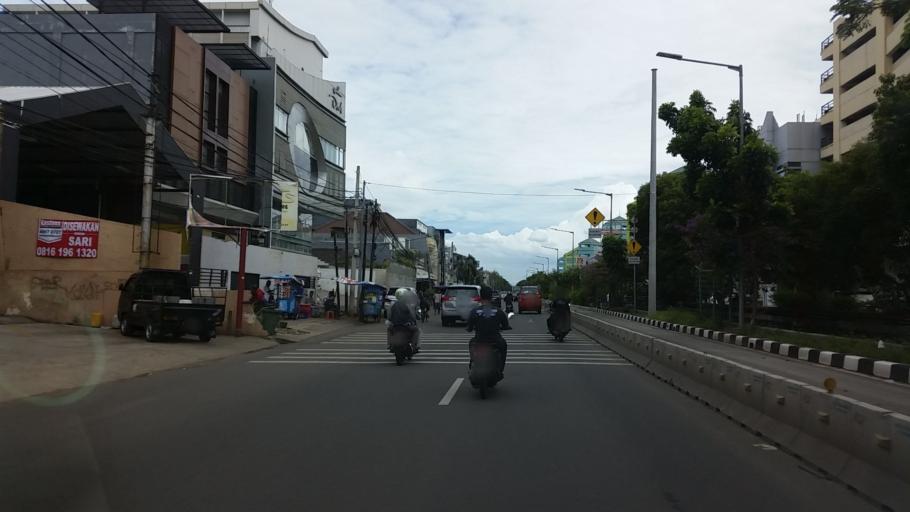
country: ID
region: Jakarta Raya
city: Jakarta
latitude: -6.1157
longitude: 106.7873
